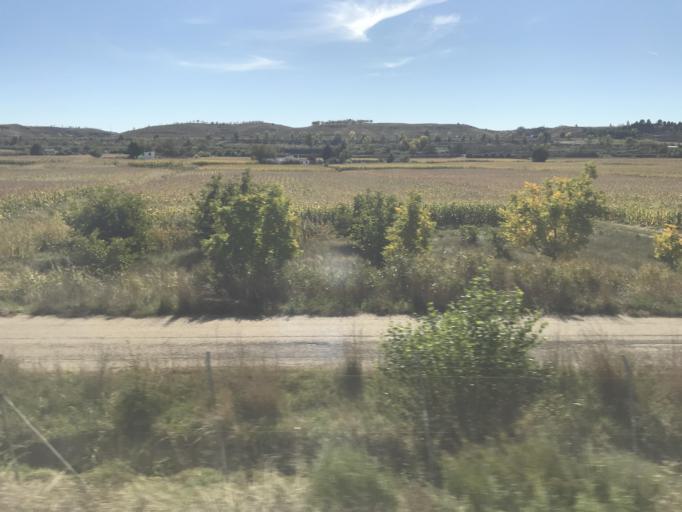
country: ES
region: Aragon
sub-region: Provincia de Zaragoza
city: Terrer
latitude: 41.3241
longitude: -1.6975
